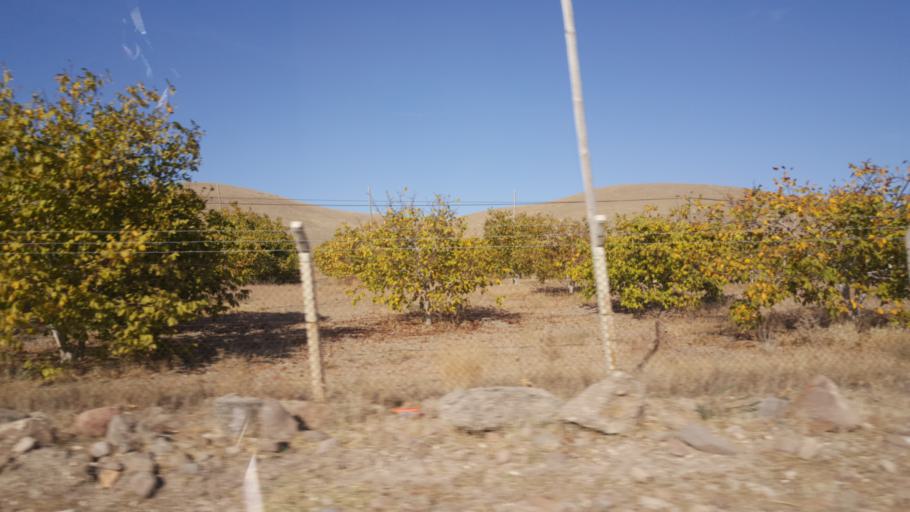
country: TR
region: Ankara
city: Altpinar
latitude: 39.1707
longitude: 32.6939
